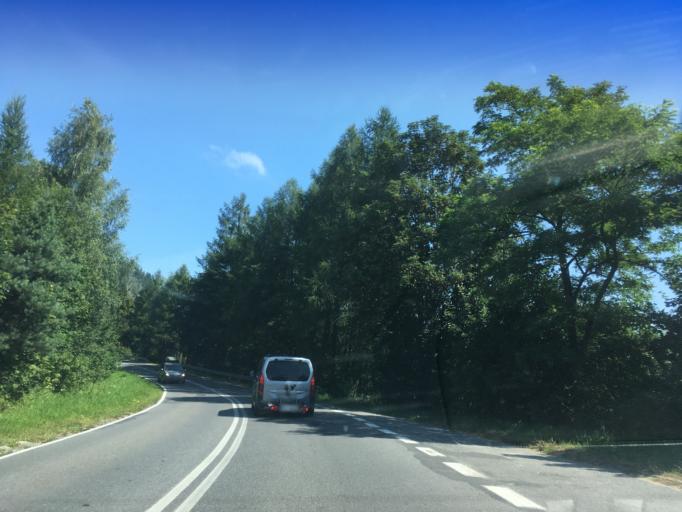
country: PL
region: Lesser Poland Voivodeship
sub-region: Powiat nowotarski
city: Krosnica
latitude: 49.4079
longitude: 20.3498
